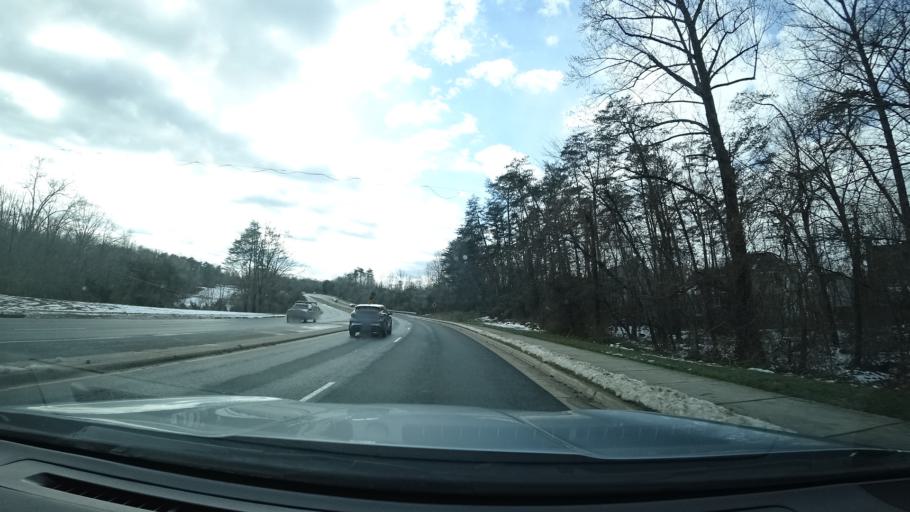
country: US
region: Virginia
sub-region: Loudoun County
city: Sugarland Run
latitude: 39.0285
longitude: -77.3629
